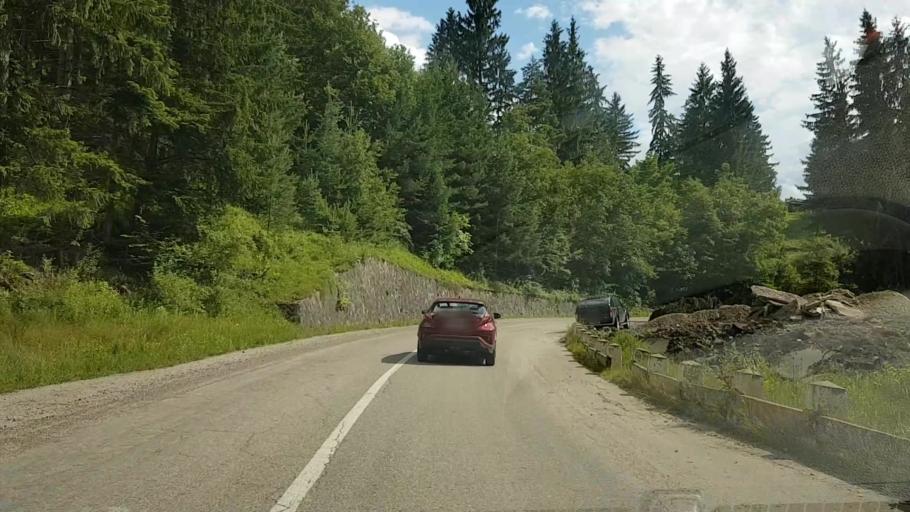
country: RO
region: Neamt
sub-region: Comuna Hangu
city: Hangu
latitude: 47.0142
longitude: 26.0829
